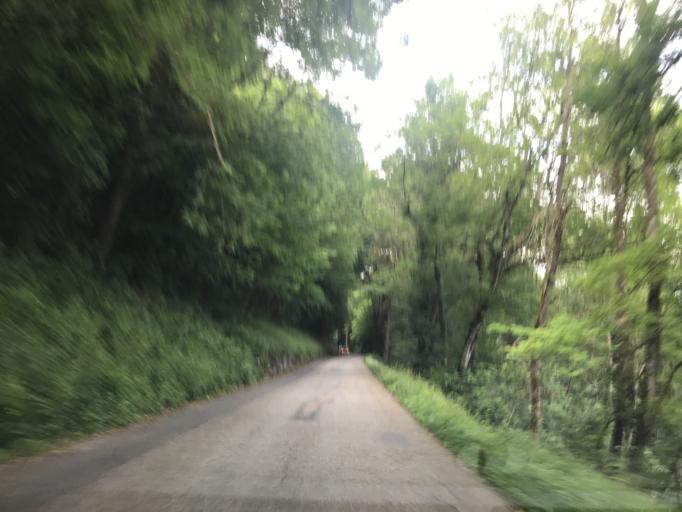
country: FR
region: Rhone-Alpes
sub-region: Departement de la Savoie
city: Mercury
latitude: 45.6767
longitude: 6.3226
